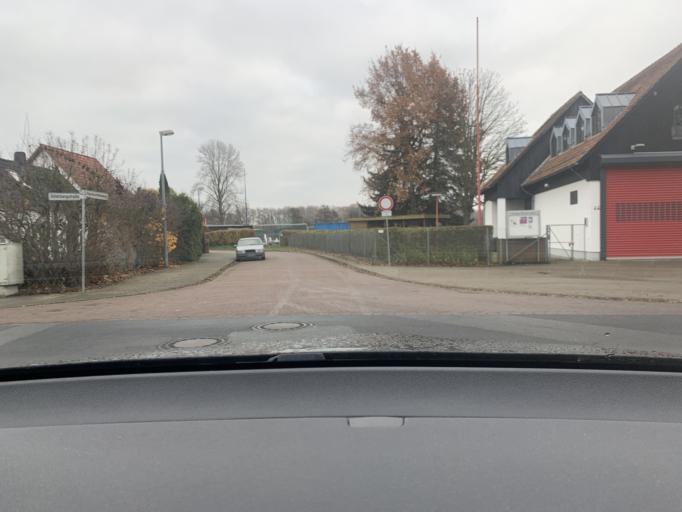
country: DE
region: Lower Saxony
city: Braunschweig
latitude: 52.3072
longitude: 10.5189
